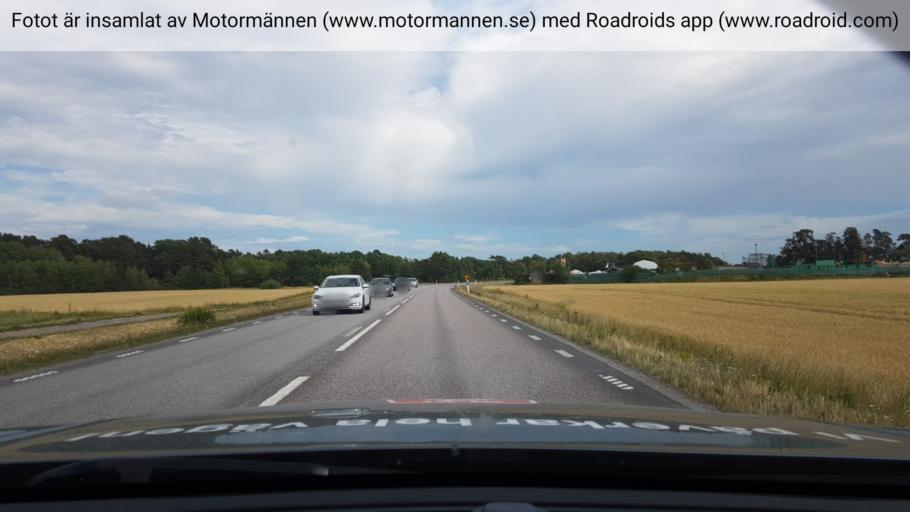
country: SE
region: Uppsala
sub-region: Uppsala Kommun
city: Uppsala
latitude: 59.8476
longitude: 17.5438
